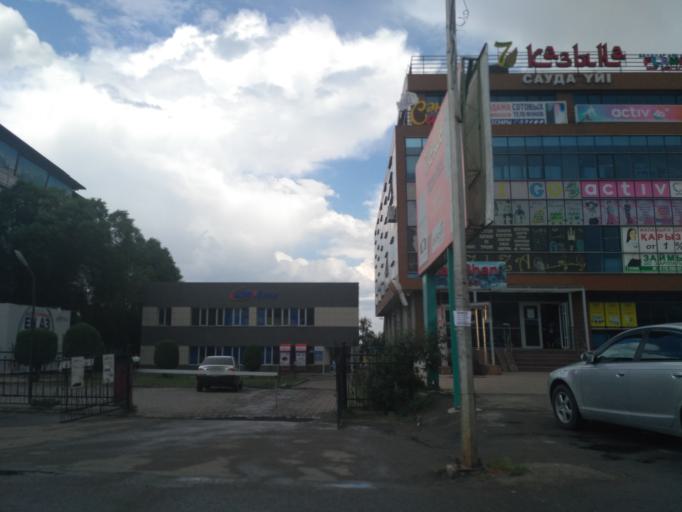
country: KZ
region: Almaty Oblysy
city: Burunday
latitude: 43.2030
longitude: 76.6204
